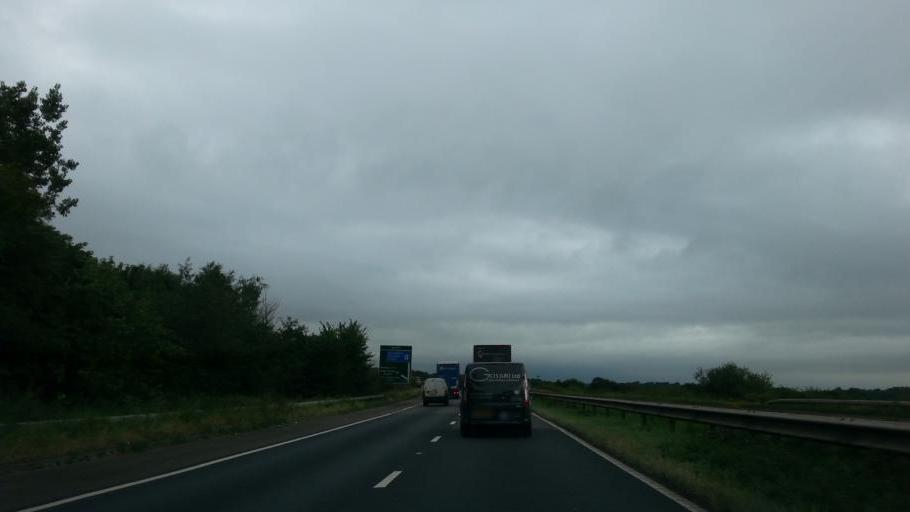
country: GB
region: England
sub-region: Nottinghamshire
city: Bircotes
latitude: 53.3777
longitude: -1.0536
